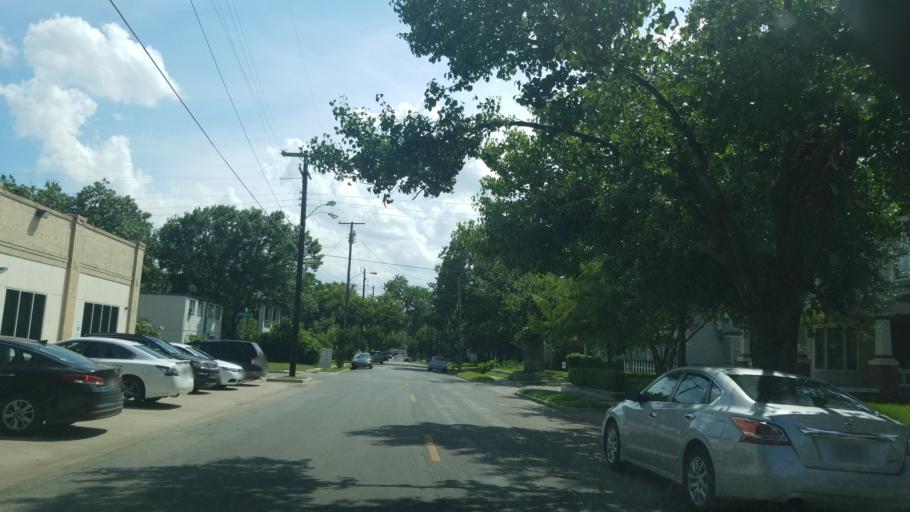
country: US
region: Texas
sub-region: Dallas County
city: Dallas
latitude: 32.7977
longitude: -96.7686
